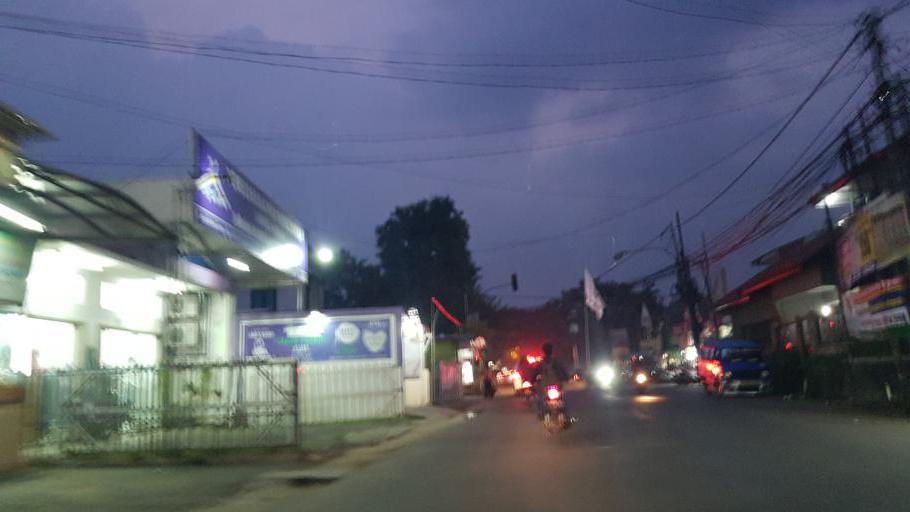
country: ID
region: West Java
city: Pamulang
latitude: -6.3402
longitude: 106.7940
